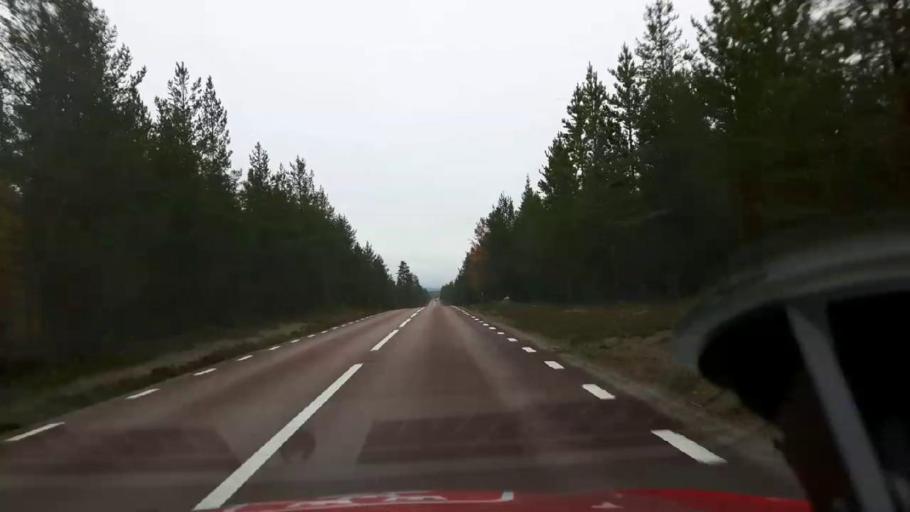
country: SE
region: Jaemtland
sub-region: Bergs Kommun
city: Hoverberg
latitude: 62.4408
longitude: 14.5791
